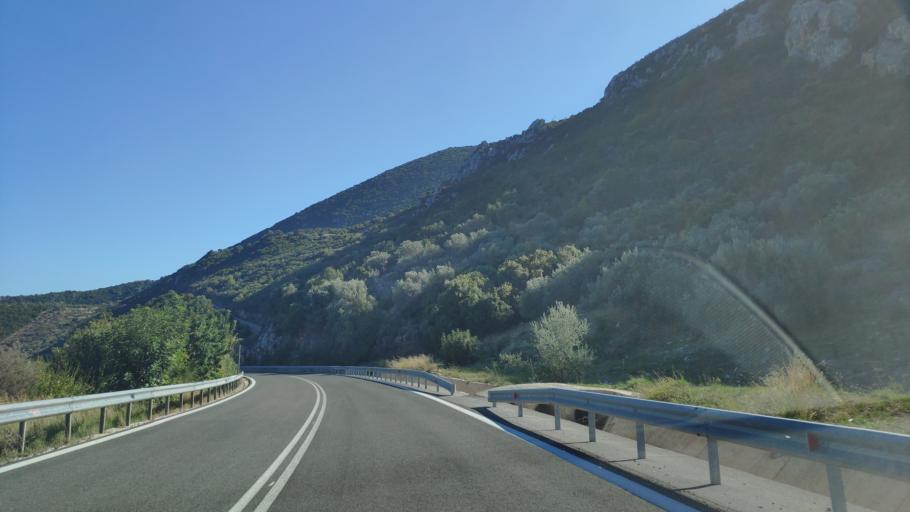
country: GR
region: Peloponnese
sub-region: Nomos Argolidos
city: Didyma
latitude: 37.5567
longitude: 23.2592
